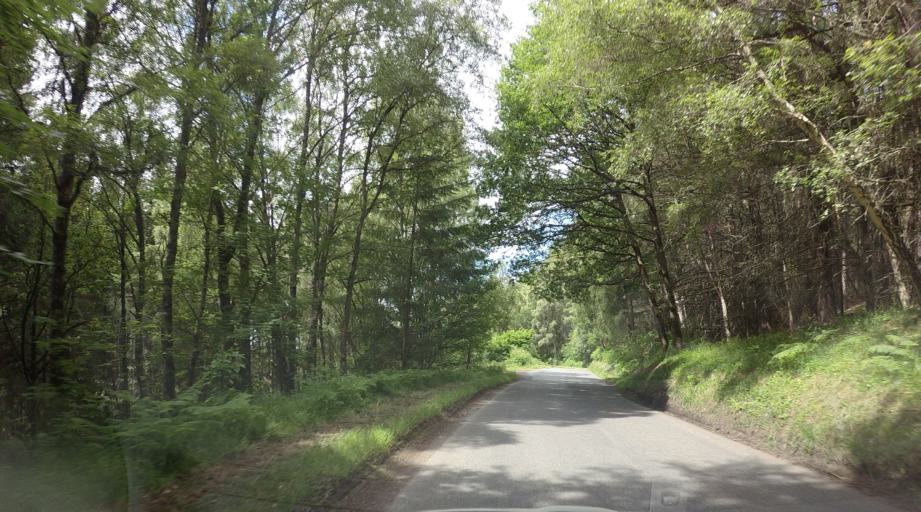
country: GB
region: Scotland
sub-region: Perth and Kinross
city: Aberfeldy
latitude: 56.7187
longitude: -3.8854
